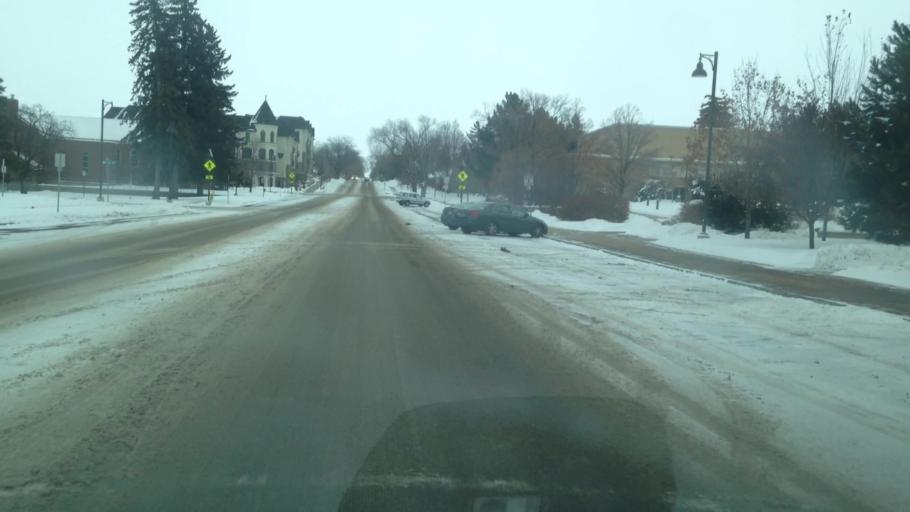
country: US
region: Idaho
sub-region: Madison County
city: Rexburg
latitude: 43.8218
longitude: -111.7834
